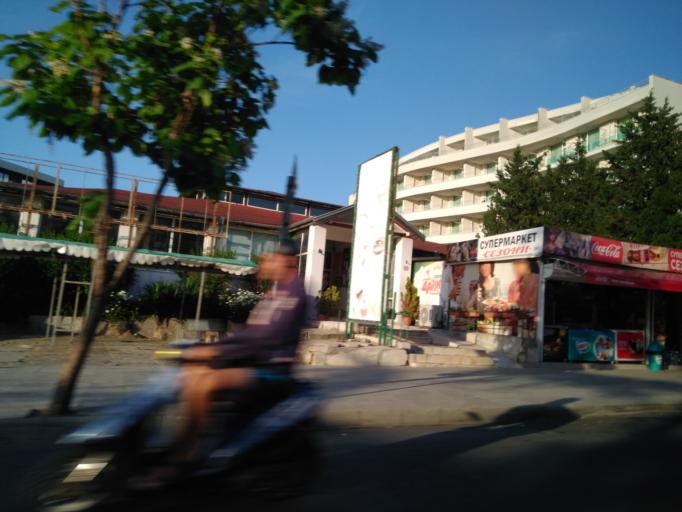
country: BG
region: Burgas
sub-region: Obshtina Nesebur
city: Nesebar
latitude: 42.6650
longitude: 27.7156
